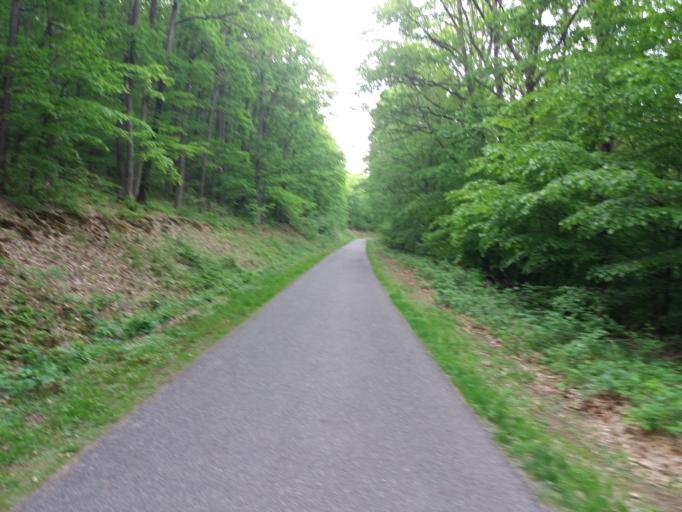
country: HU
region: Borsod-Abauj-Zemplen
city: Gonc
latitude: 48.4991
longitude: 21.3904
